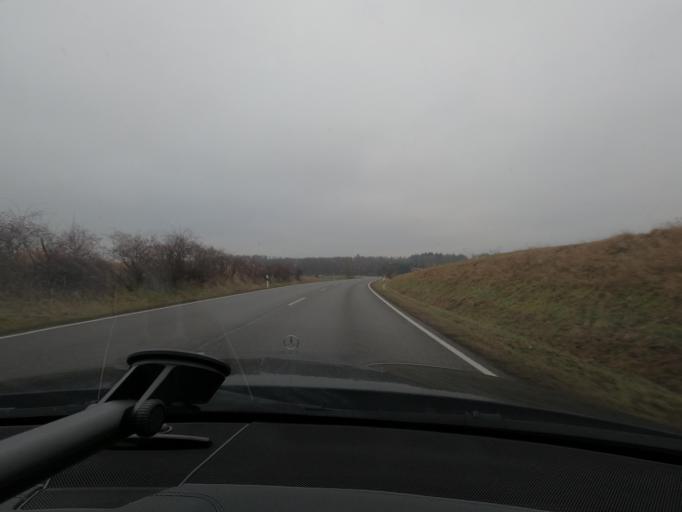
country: DE
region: Hesse
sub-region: Regierungsbezirk Kassel
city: Wolfhagen
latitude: 51.3382
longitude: 9.1075
